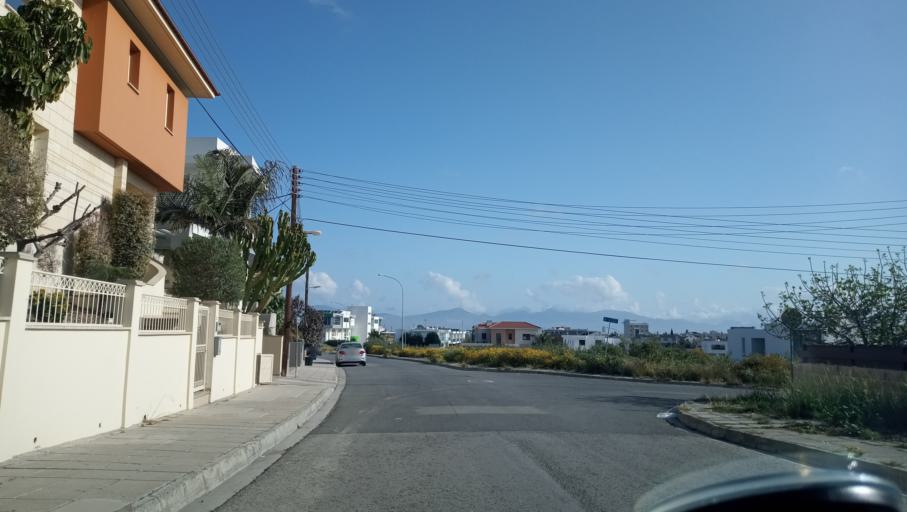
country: CY
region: Lefkosia
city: Tseri
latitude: 35.1163
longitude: 33.3338
